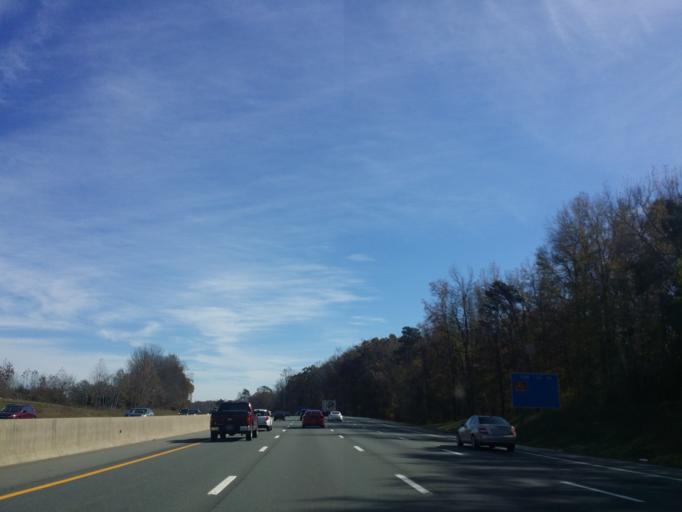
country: US
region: North Carolina
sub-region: Alamance County
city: Haw River
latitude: 36.0660
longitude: -79.3233
